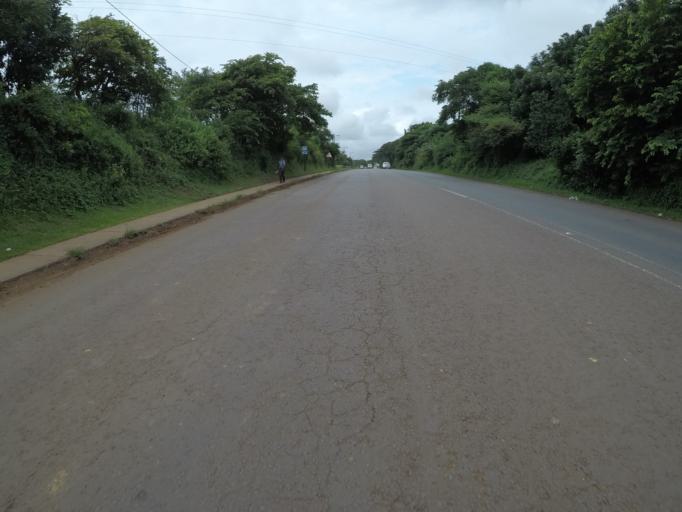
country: ZA
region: KwaZulu-Natal
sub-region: uThungulu District Municipality
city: Empangeni
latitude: -28.7769
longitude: 31.8843
